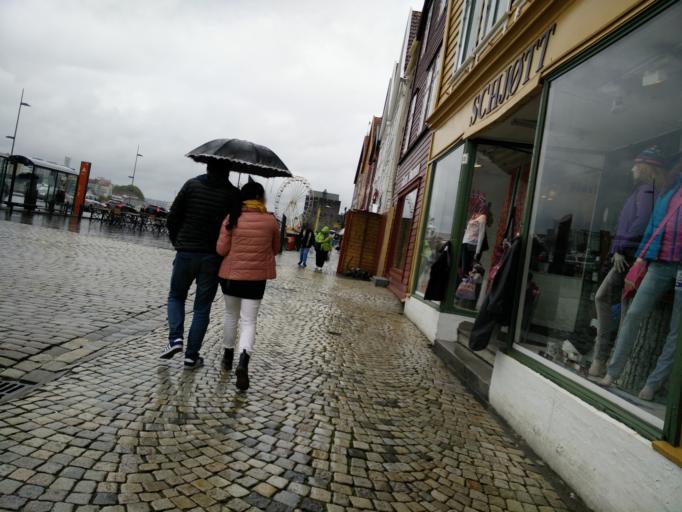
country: NO
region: Hordaland
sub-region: Bergen
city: Bergen
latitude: 60.3972
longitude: 5.3232
